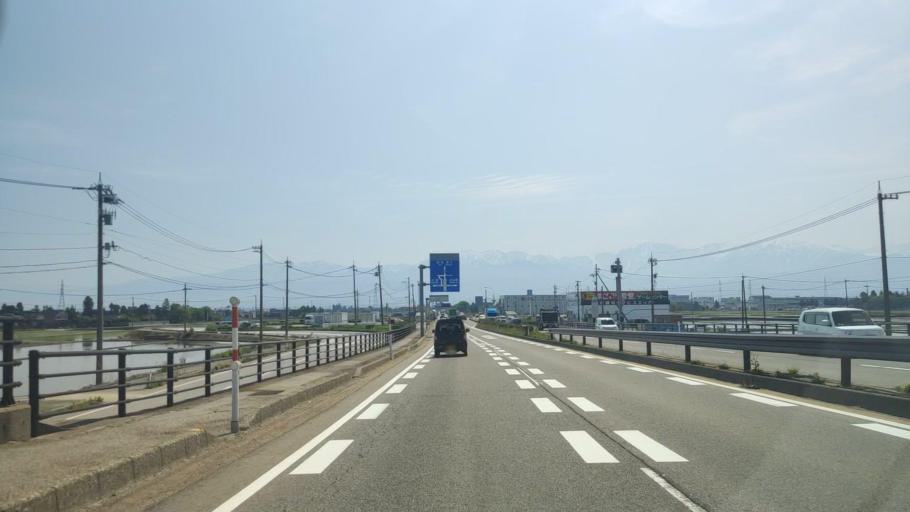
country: JP
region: Toyama
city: Toyama-shi
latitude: 36.7181
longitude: 137.2794
